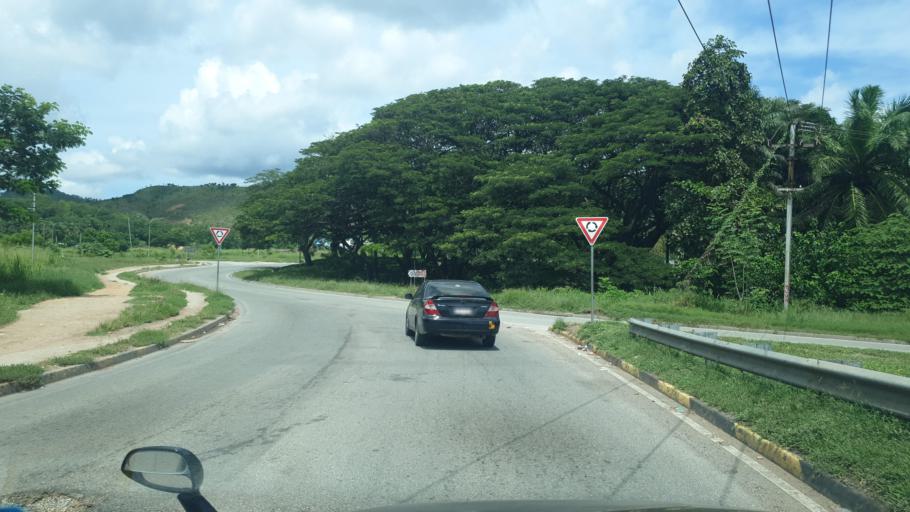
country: PG
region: National Capital
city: Port Moresby
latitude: -9.3984
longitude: 147.1596
